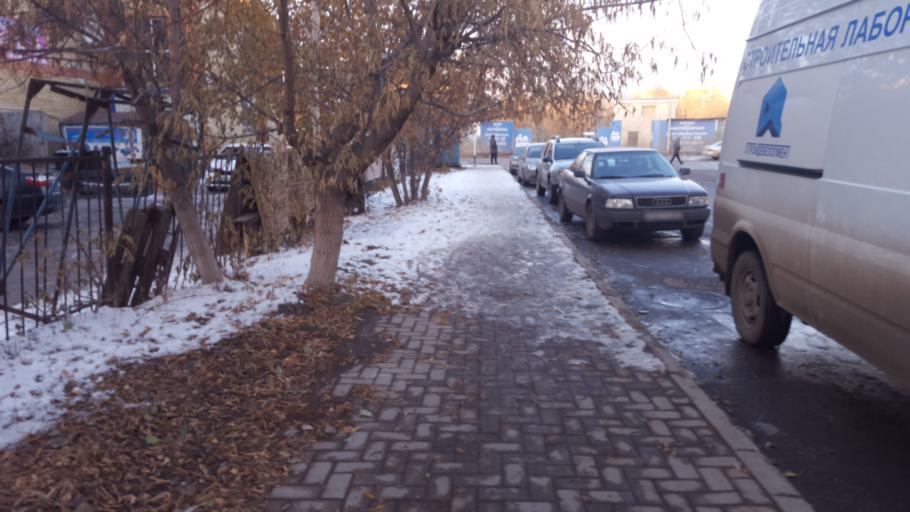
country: KZ
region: Astana Qalasy
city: Astana
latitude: 51.1586
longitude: 71.4920
